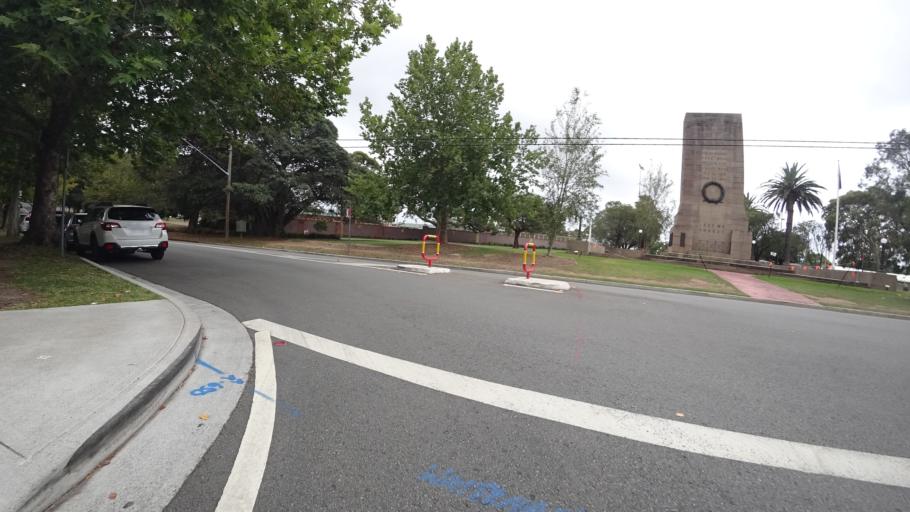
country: AU
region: New South Wales
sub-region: North Sydney
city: North Sydney
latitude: -33.8333
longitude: 151.2099
